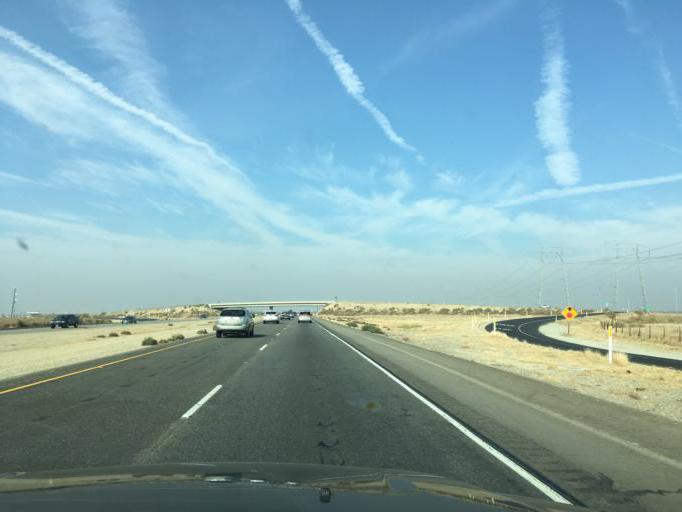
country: US
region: California
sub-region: Kern County
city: Buttonwillow
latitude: 35.4981
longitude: -119.5325
